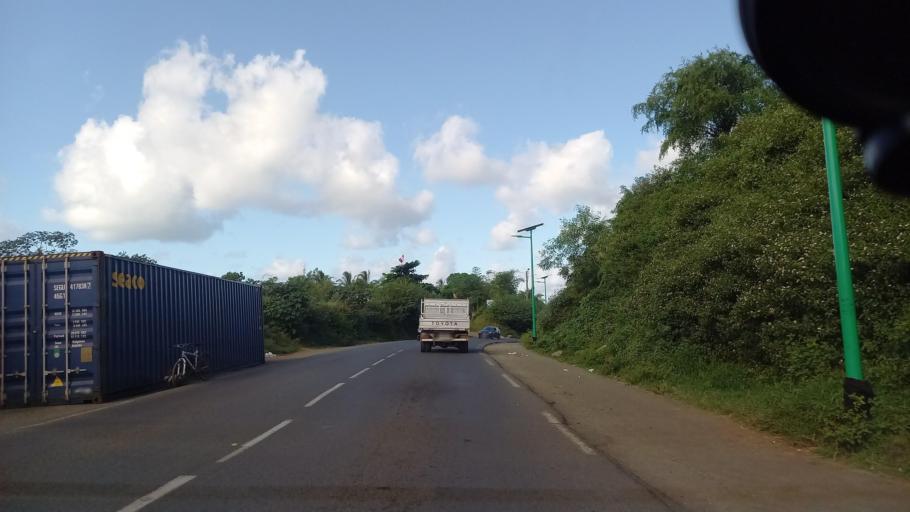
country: YT
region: Koungou
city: Koungou
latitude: -12.7448
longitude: 45.2228
